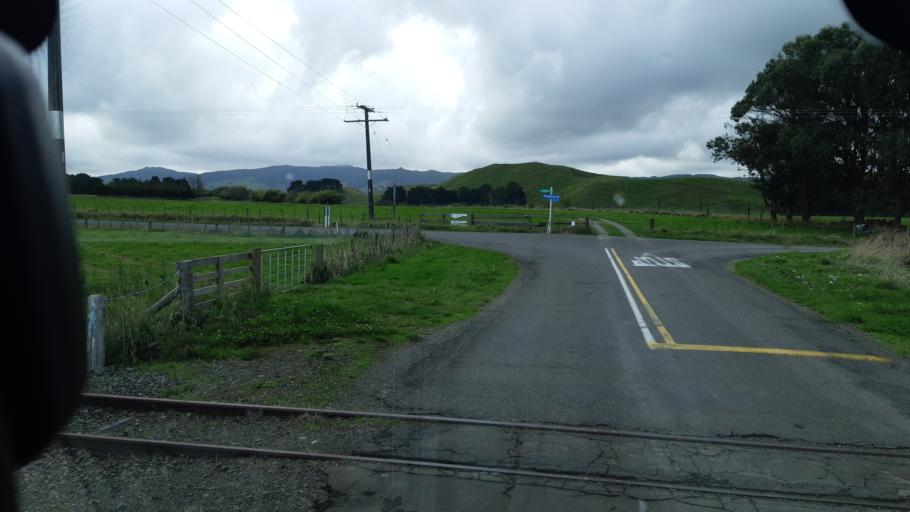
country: NZ
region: Manawatu-Wanganui
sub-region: Palmerston North City
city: Palmerston North
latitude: -40.5364
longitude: 175.7272
